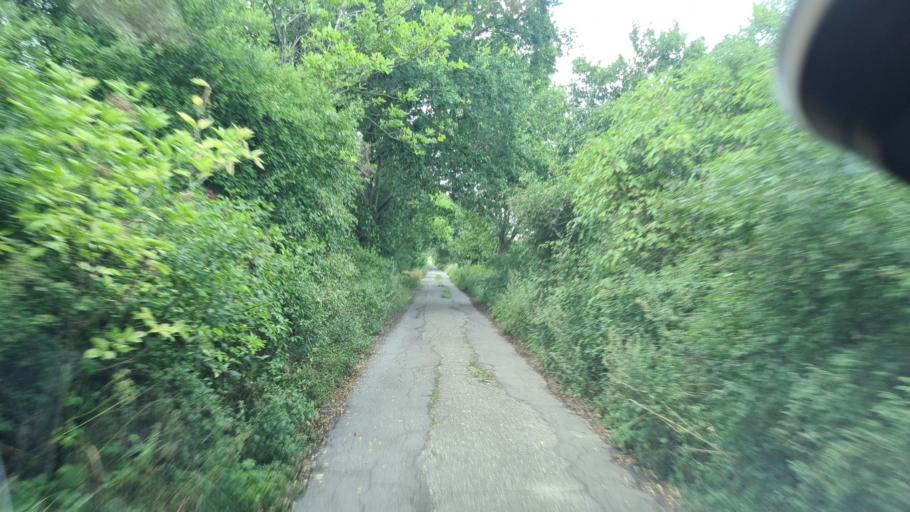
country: DE
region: Brandenburg
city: Drebkau
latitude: 51.6343
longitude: 14.2915
